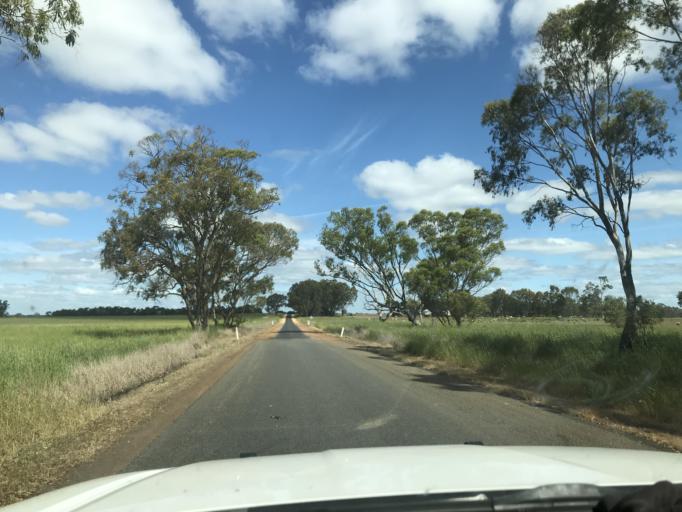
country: AU
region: South Australia
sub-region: Naracoorte and Lucindale
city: Naracoorte
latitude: -36.9940
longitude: 141.2924
